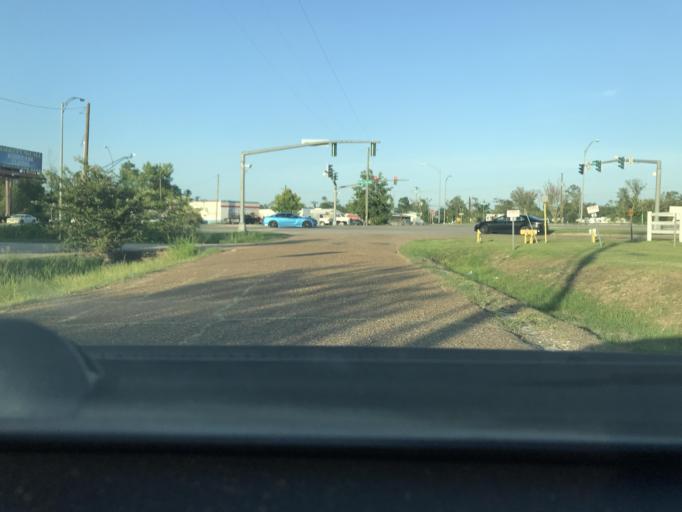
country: US
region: Louisiana
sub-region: Calcasieu Parish
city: Moss Bluff
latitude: 30.2655
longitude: -93.1815
